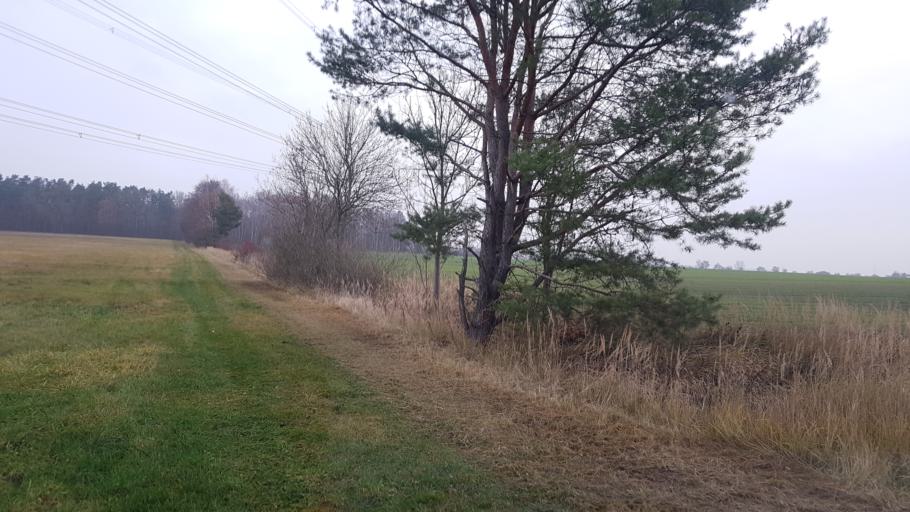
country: DE
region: Brandenburg
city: Doberlug-Kirchhain
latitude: 51.6278
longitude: 13.5353
